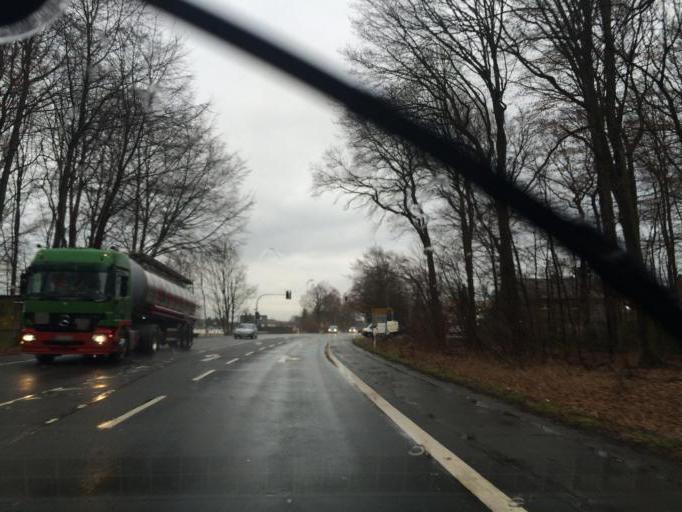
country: DE
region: North Rhine-Westphalia
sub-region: Regierungsbezirk Munster
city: Gladbeck
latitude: 51.6047
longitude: 6.9604
